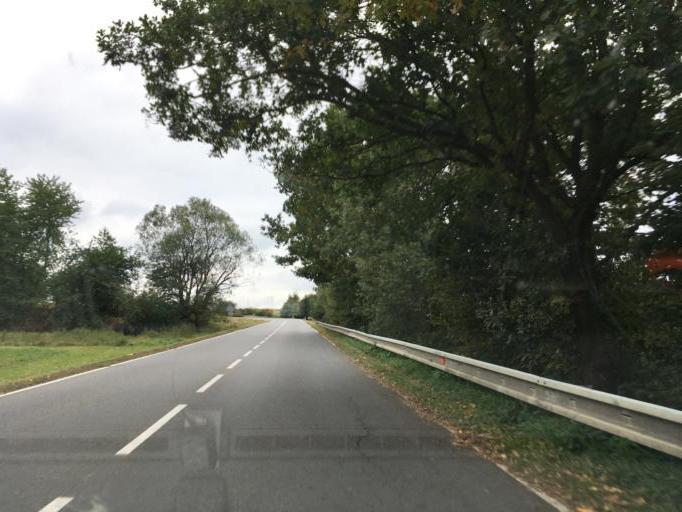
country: CZ
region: Vysocina
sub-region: Okres Pelhrimov
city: Zeliv
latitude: 49.5084
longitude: 15.1787
